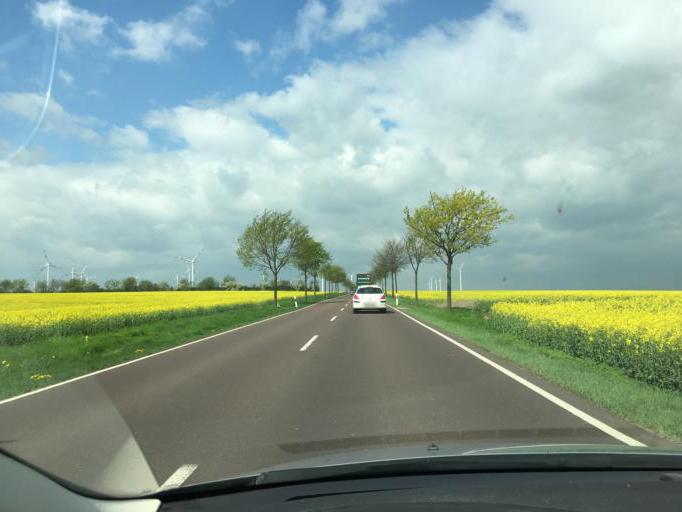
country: DE
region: Saxony-Anhalt
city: Sandersleben
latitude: 51.7203
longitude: 11.5989
